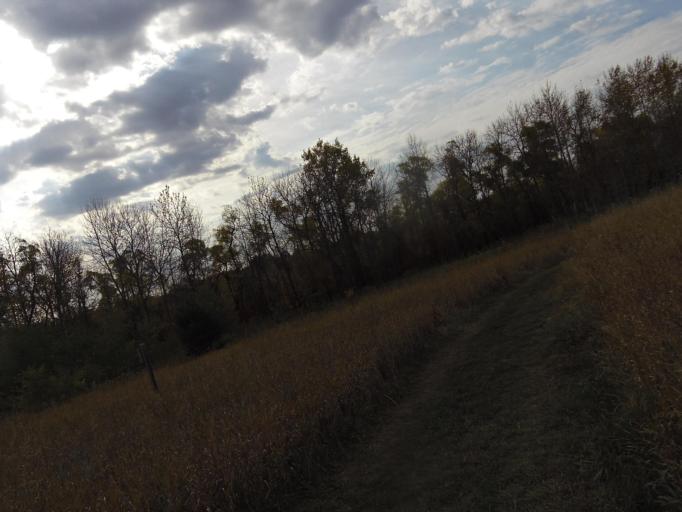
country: US
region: North Dakota
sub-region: Pembina County
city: Cavalier
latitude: 48.7798
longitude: -97.7448
